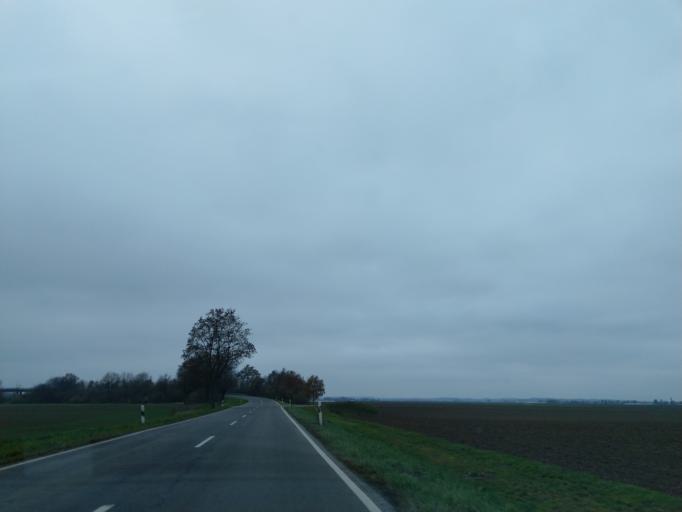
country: DE
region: Bavaria
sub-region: Lower Bavaria
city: Otzing
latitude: 48.7795
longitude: 12.7964
